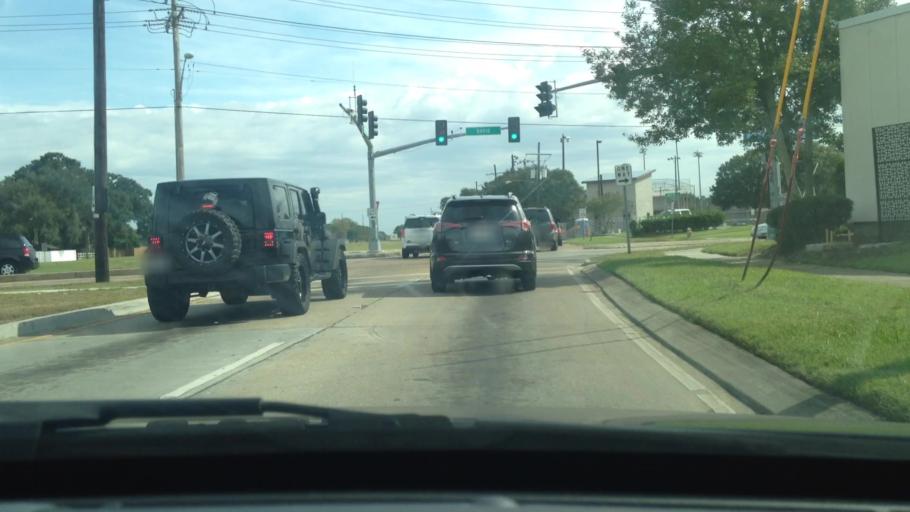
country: US
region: Louisiana
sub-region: Jefferson Parish
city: River Ridge
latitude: 29.9848
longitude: -90.2138
